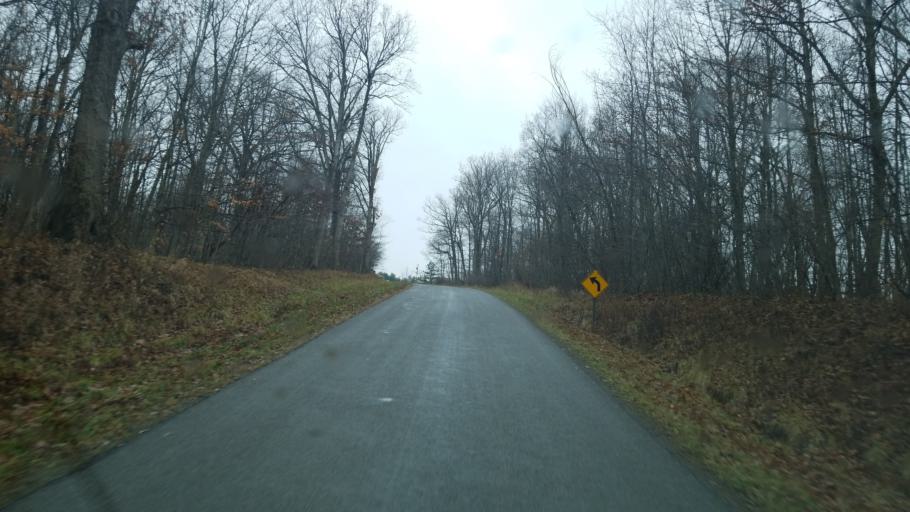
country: US
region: Ohio
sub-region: Logan County
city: Northwood
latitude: 40.4687
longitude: -83.6567
